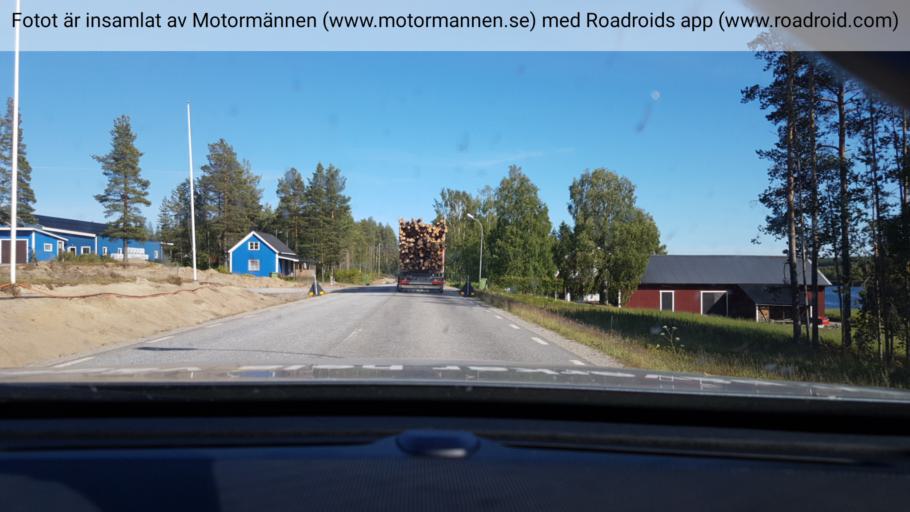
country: SE
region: Vaesterbotten
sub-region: Vindelns Kommun
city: Vindeln
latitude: 64.2163
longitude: 19.3874
